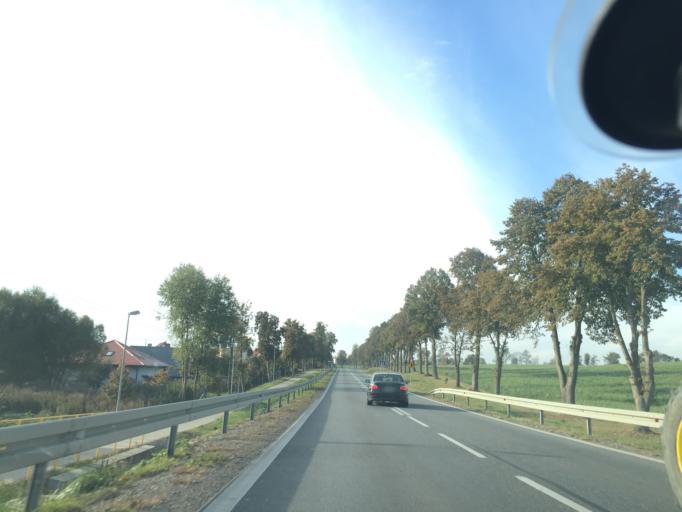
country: PL
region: Warmian-Masurian Voivodeship
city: Dobre Miasto
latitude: 53.9978
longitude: 20.4004
